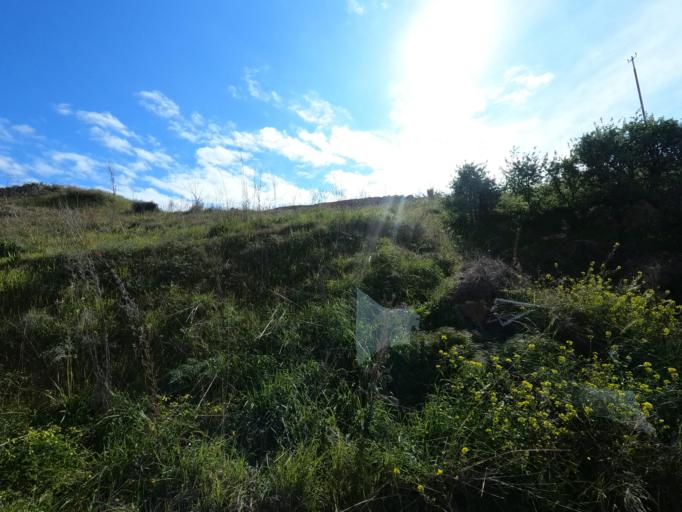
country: CY
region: Lefkosia
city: Lefka
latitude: 35.1007
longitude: 32.8863
